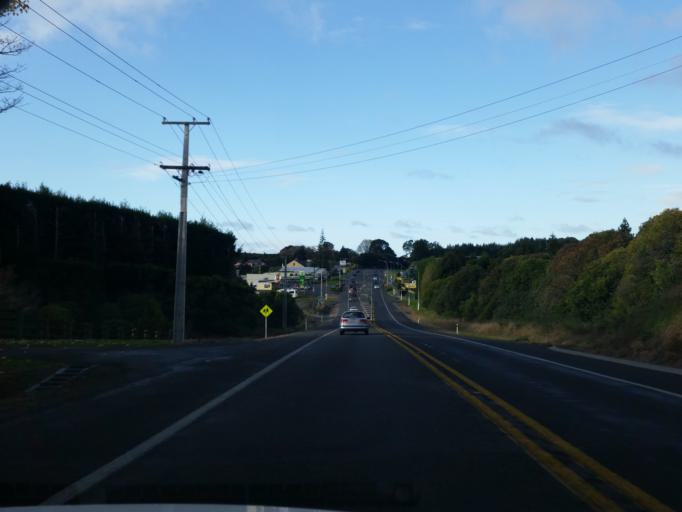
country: NZ
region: Bay of Plenty
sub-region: Tauranga City
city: Tauranga
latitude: -37.6967
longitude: 176.0689
